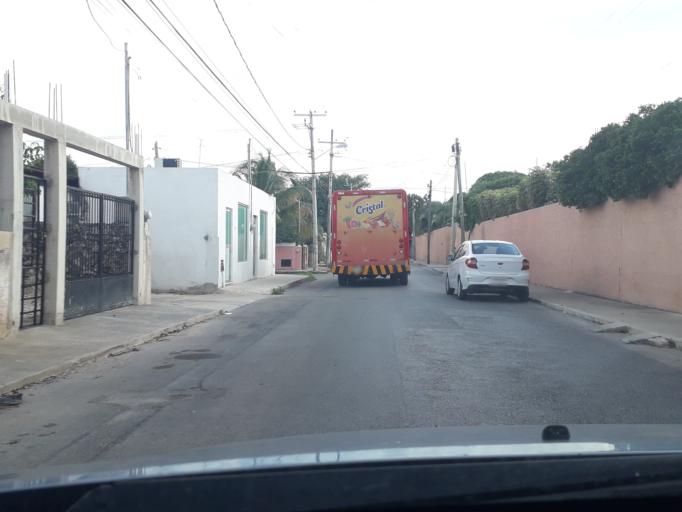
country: MX
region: Yucatan
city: Merida
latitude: 21.0097
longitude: -89.6364
